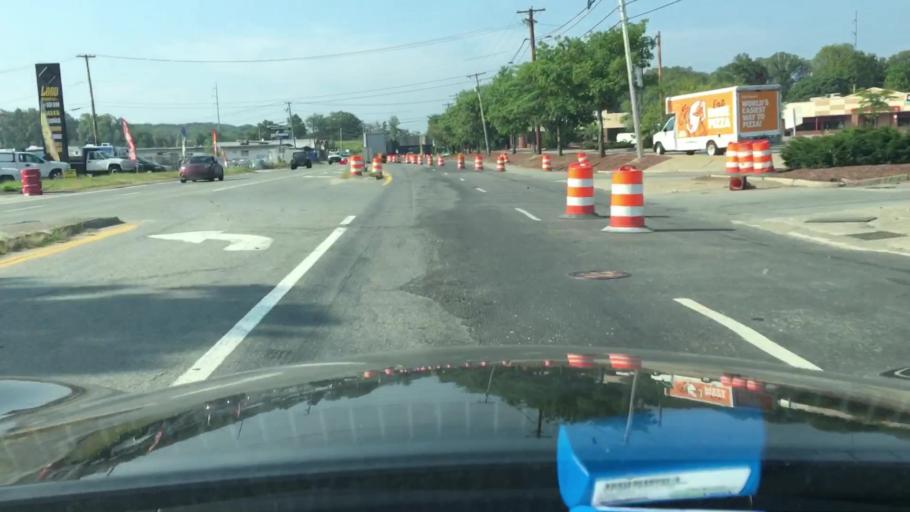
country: US
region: Massachusetts
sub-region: Worcester County
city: Sunderland
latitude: 42.2397
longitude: -71.7457
